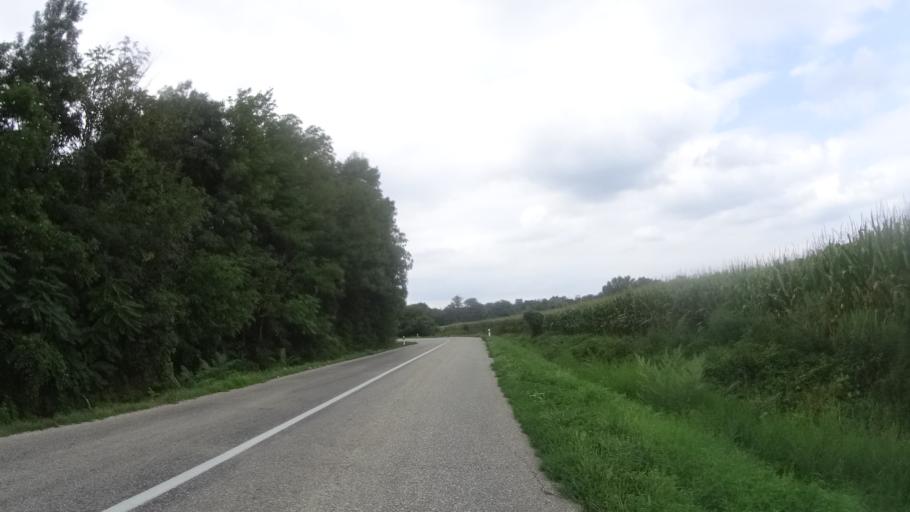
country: SK
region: Trnavsky
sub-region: Okres Dunajska Streda
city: Velky Meder
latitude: 47.7541
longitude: 17.7976
